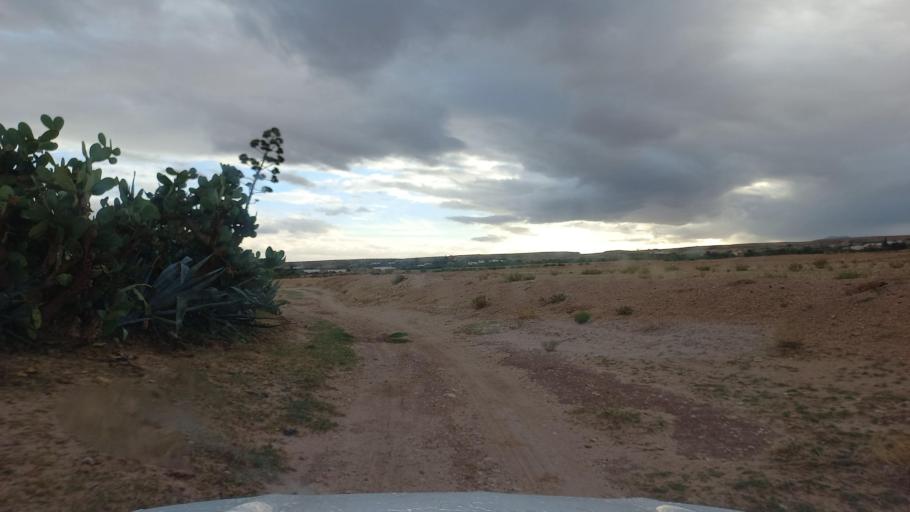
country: TN
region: Al Qasrayn
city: Kasserine
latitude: 35.2714
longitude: 8.9368
